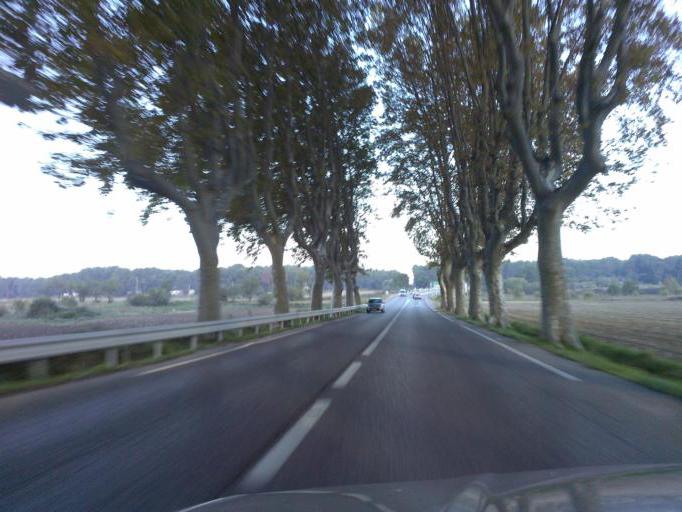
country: FR
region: Provence-Alpes-Cote d'Azur
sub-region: Departement des Bouches-du-Rhone
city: Saint-Cannat
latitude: 43.6362
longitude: 5.2798
